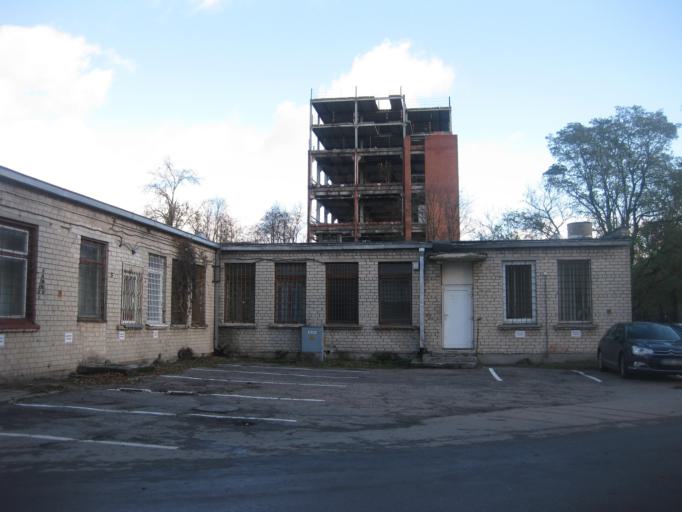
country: LT
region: Kauno apskritis
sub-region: Kaunas
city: Silainiai
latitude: 54.9149
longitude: 23.8932
